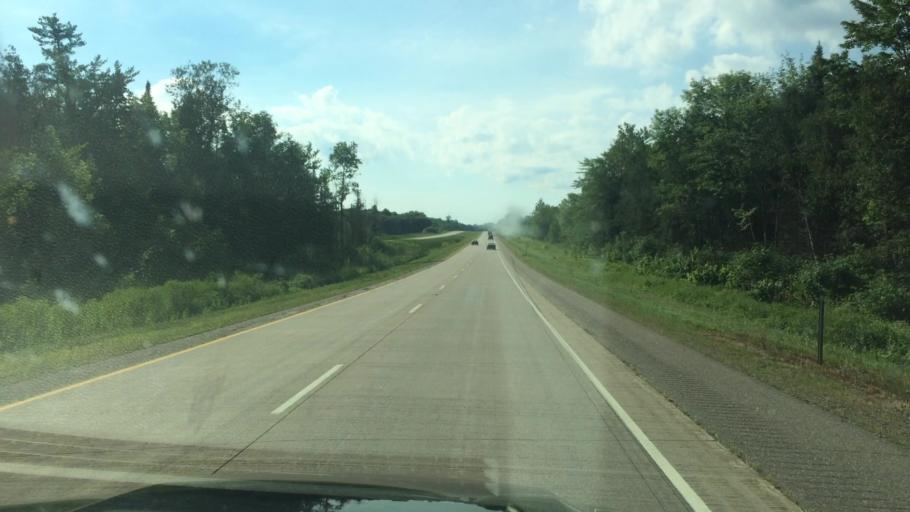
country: US
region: Wisconsin
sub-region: Shawano County
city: Wittenberg
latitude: 44.8161
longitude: -89.0494
